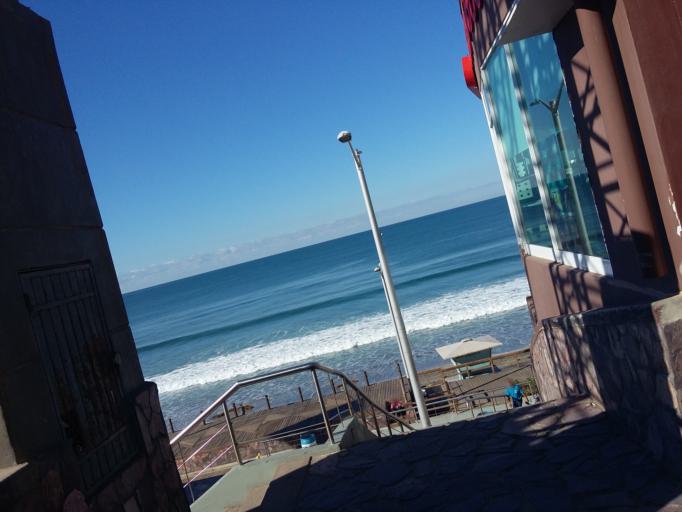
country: US
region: California
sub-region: San Diego County
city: Imperial Beach
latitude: 32.5311
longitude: -117.1232
